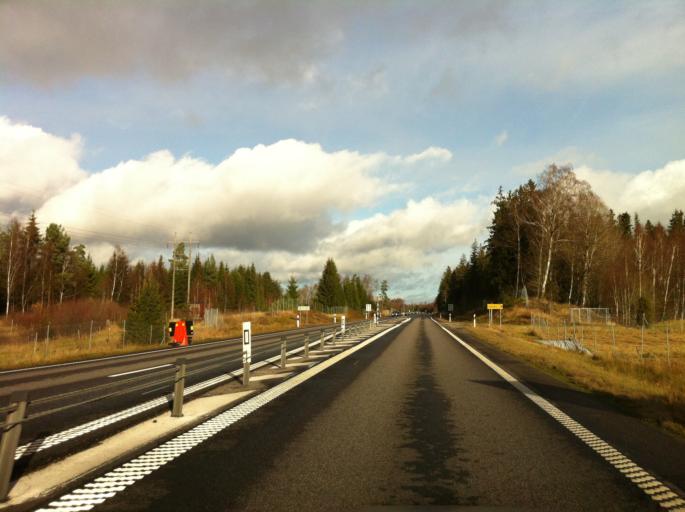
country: SE
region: Kronoberg
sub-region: Almhults Kommun
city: AElmhult
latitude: 56.5013
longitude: 14.1141
